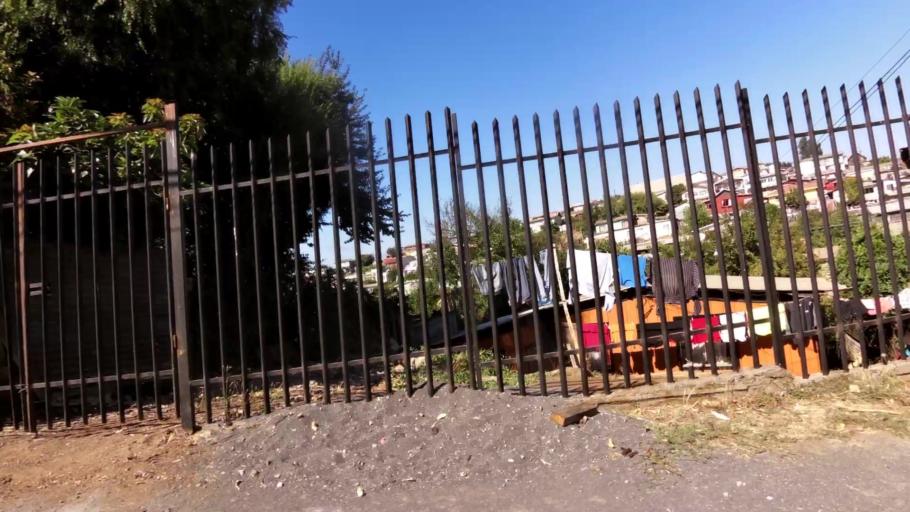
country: CL
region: Biobio
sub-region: Provincia de Concepcion
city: Concepcion
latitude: -36.7951
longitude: -73.0463
